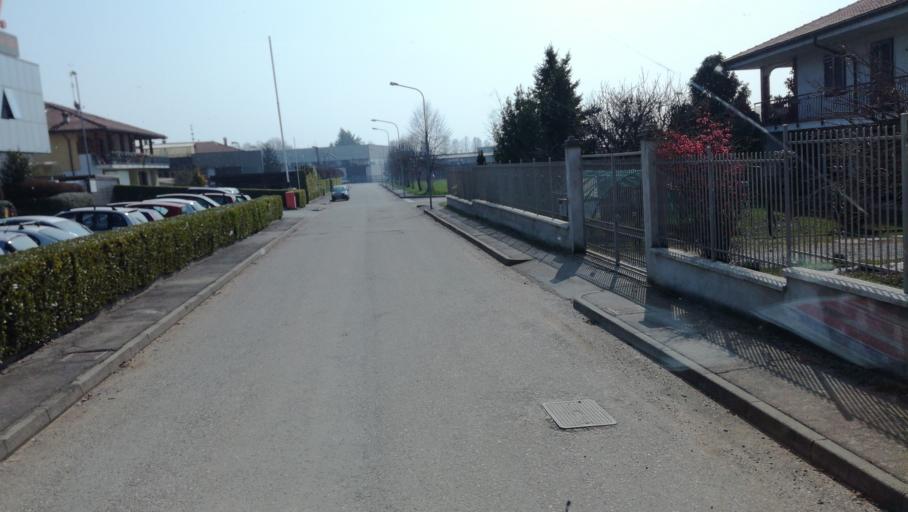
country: IT
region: Piedmont
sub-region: Provincia di Novara
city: Grignasco
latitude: 45.6733
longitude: 8.3516
